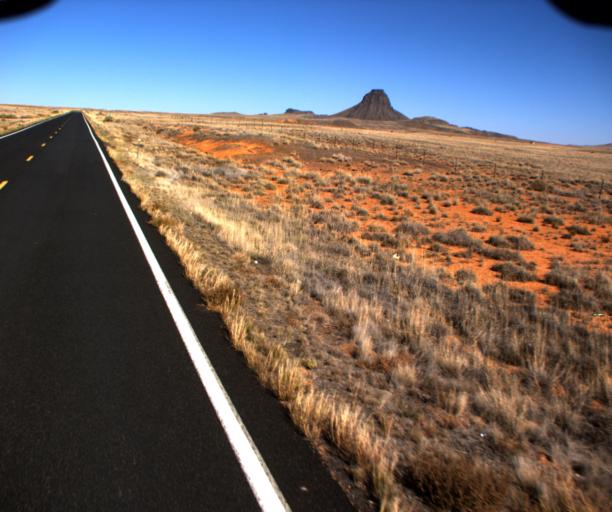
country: US
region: Arizona
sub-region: Navajo County
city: Dilkon
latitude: 35.2706
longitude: -110.4293
